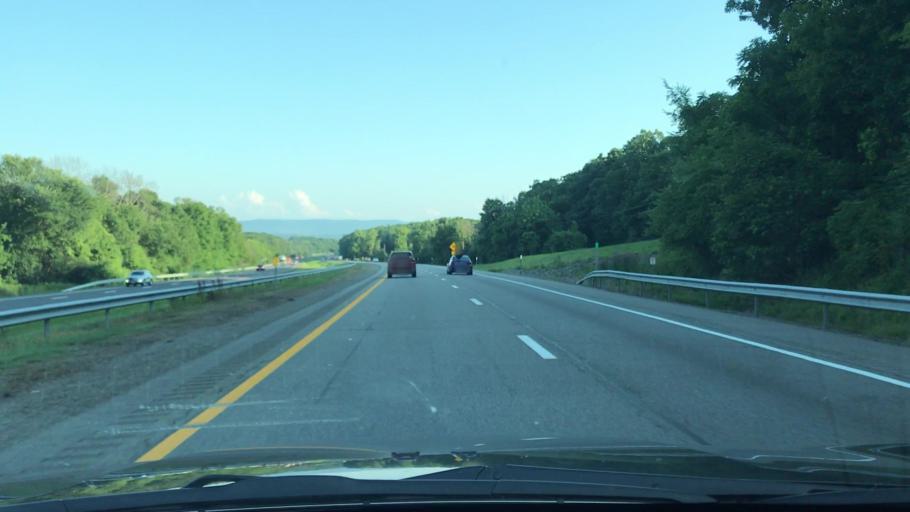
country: US
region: New York
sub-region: Orange County
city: Gardnertown
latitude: 41.5502
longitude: -74.0805
